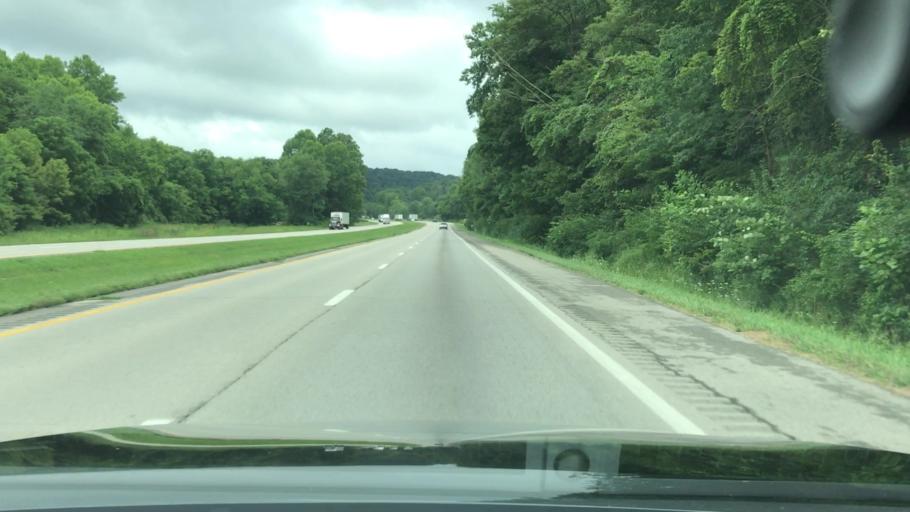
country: US
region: Ohio
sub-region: Pike County
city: Waverly
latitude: 39.1959
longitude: -82.8016
